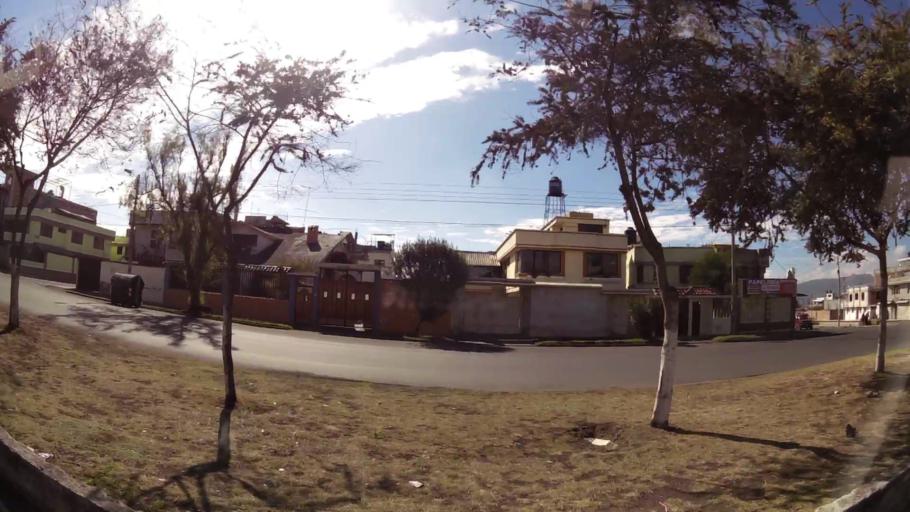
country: EC
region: Chimborazo
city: Riobamba
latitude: -1.6547
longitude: -78.6696
